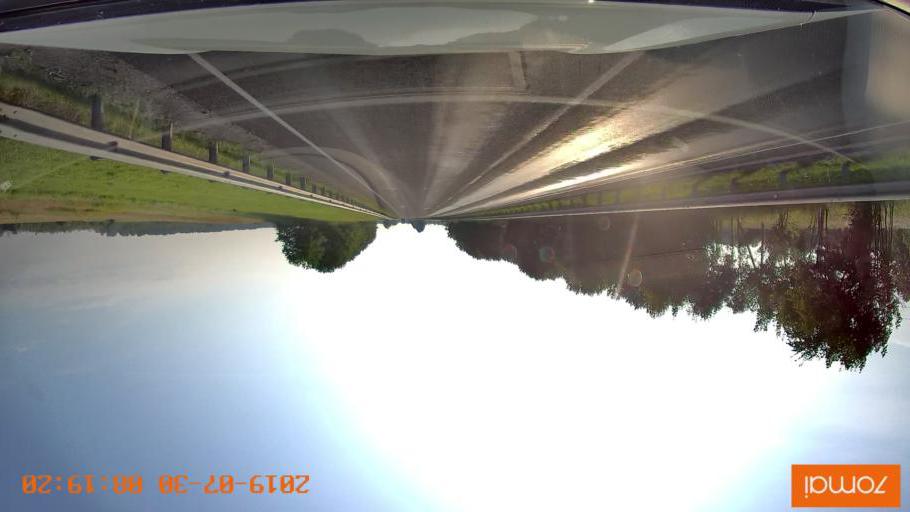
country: RU
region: Kaliningrad
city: Zheleznodorozhnyy
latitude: 54.6290
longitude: 21.4887
